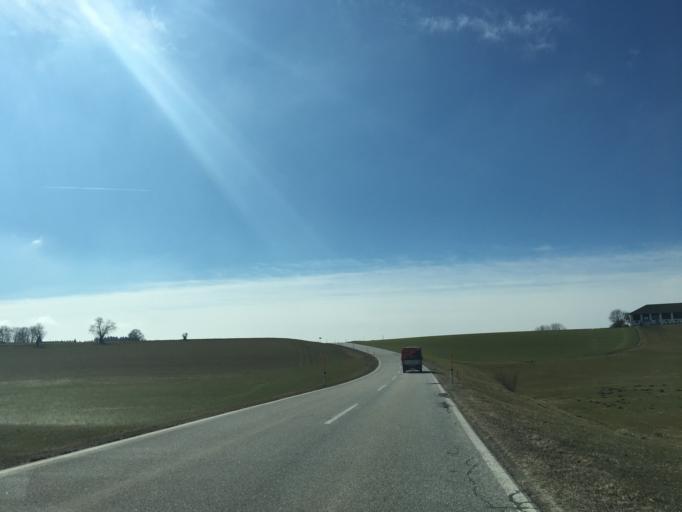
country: AT
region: Upper Austria
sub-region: Politischer Bezirk Perg
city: Sankt Georgen am Walde
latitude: 48.3143
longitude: 14.9078
